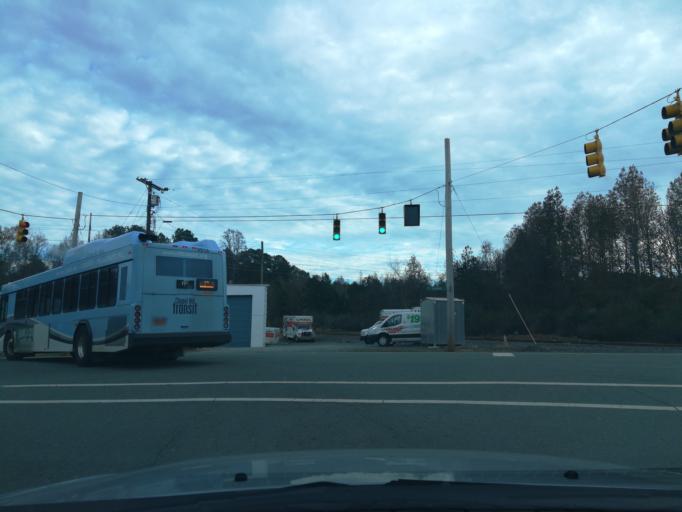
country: US
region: North Carolina
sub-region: Orange County
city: Carrboro
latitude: 35.9699
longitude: -79.0751
